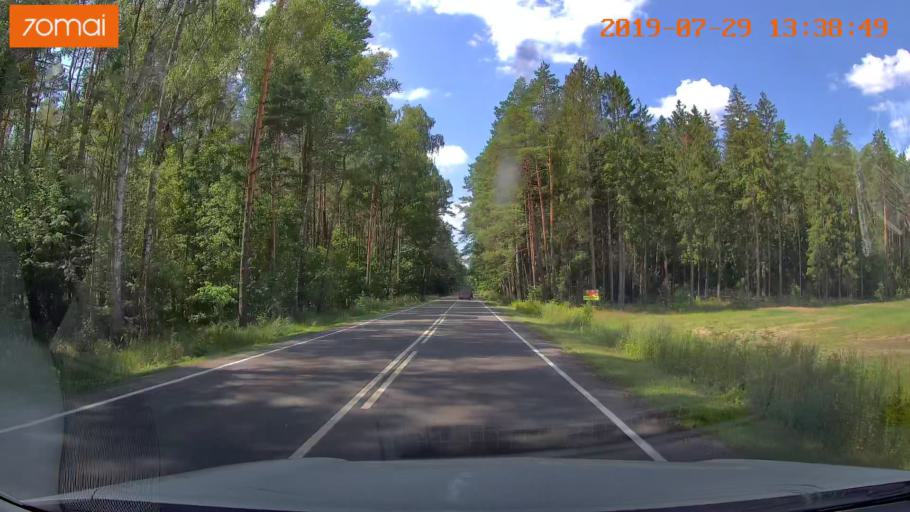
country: RU
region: Kaliningrad
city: Svetlyy
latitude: 54.7226
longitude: 20.1649
